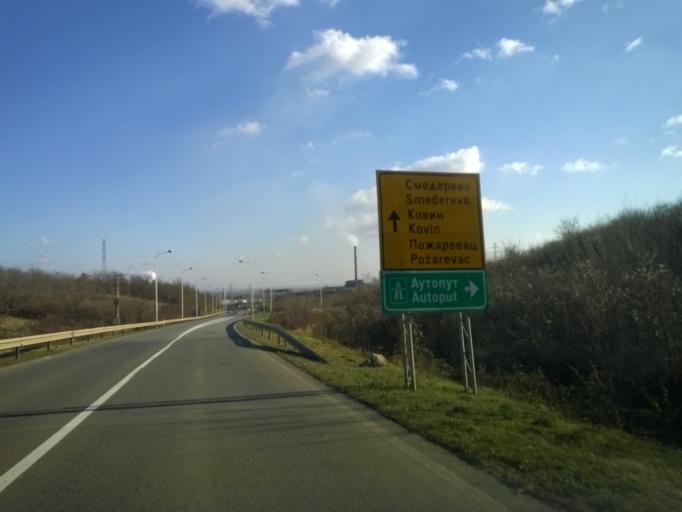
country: RS
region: Central Serbia
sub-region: Podunavski Okrug
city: Smederevo
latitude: 44.6098
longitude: 20.9522
